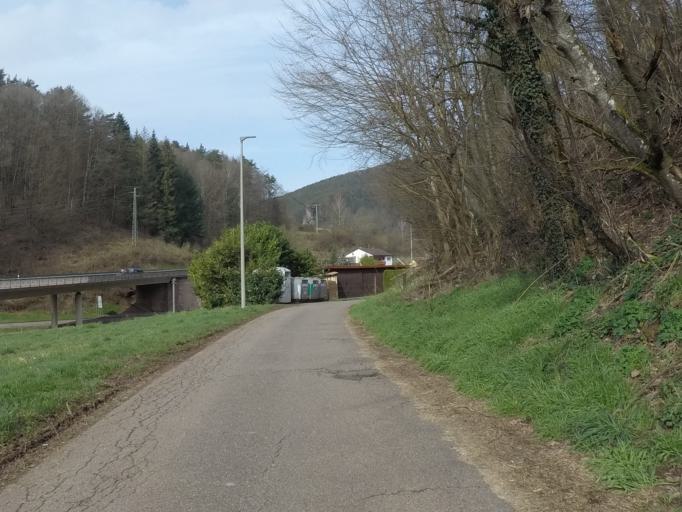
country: DE
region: Rheinland-Pfalz
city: Lug
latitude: 49.1788
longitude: 7.8986
